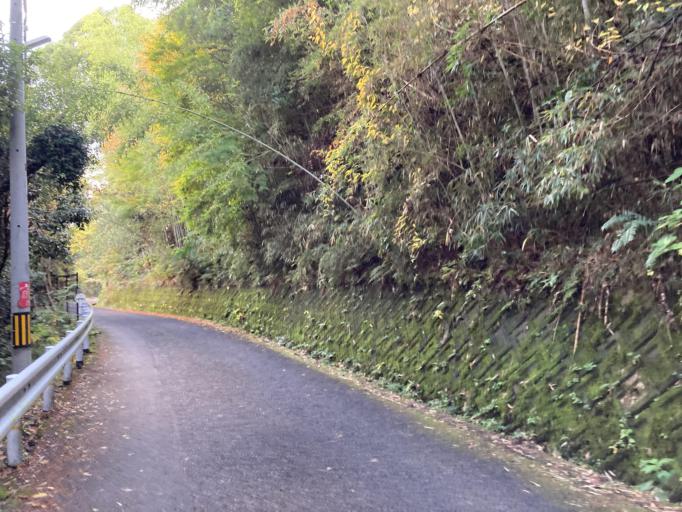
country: JP
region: Nara
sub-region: Ikoma-shi
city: Ikoma
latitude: 34.6809
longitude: 135.6915
